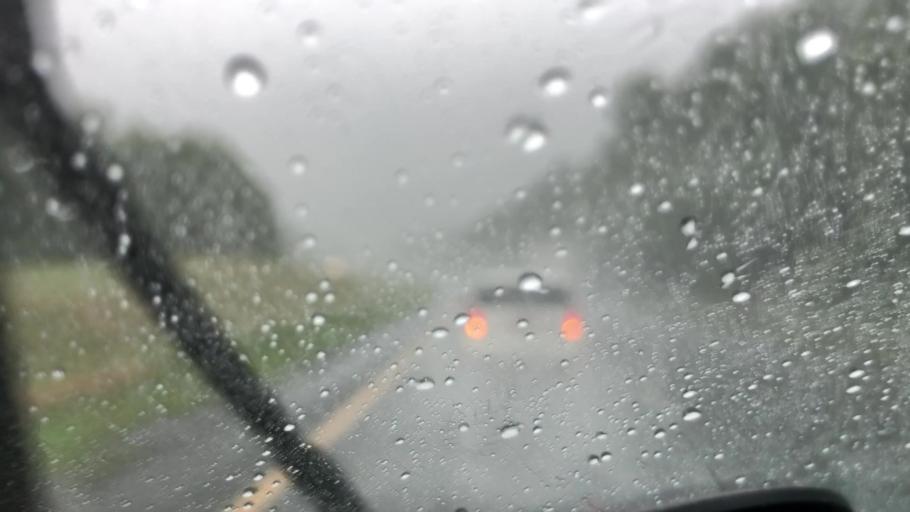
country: US
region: Massachusetts
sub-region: Hampden County
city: Westfield
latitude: 42.1569
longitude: -72.8002
